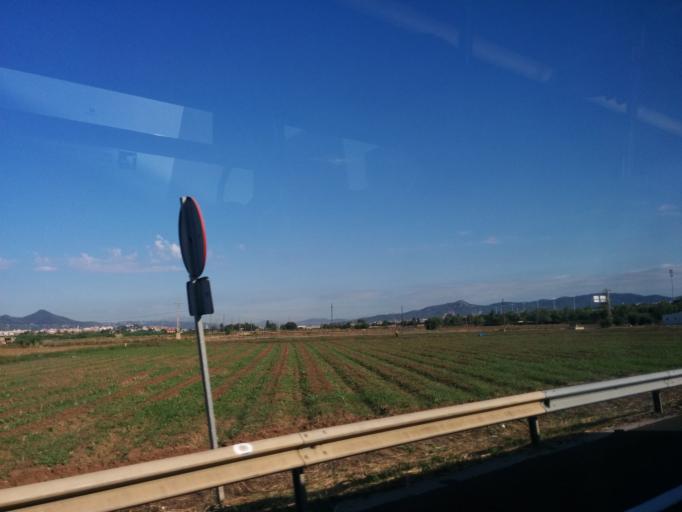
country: ES
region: Catalonia
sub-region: Provincia de Barcelona
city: El Prat de Llobregat
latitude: 41.3186
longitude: 2.0721
